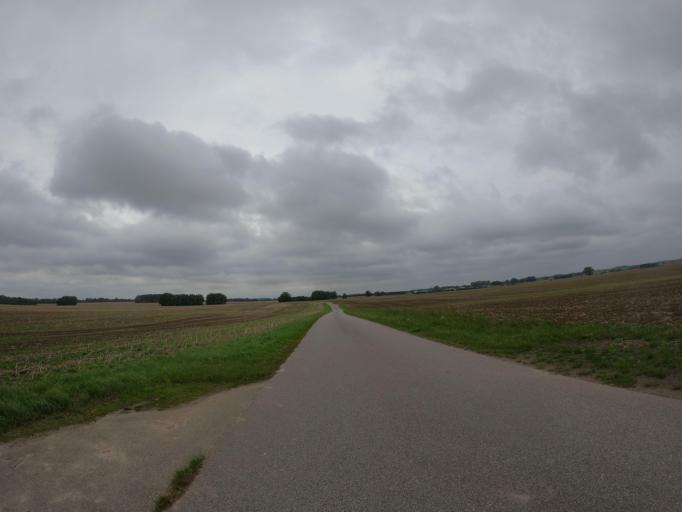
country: DE
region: Mecklenburg-Vorpommern
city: Garz
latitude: 54.2931
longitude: 13.3259
